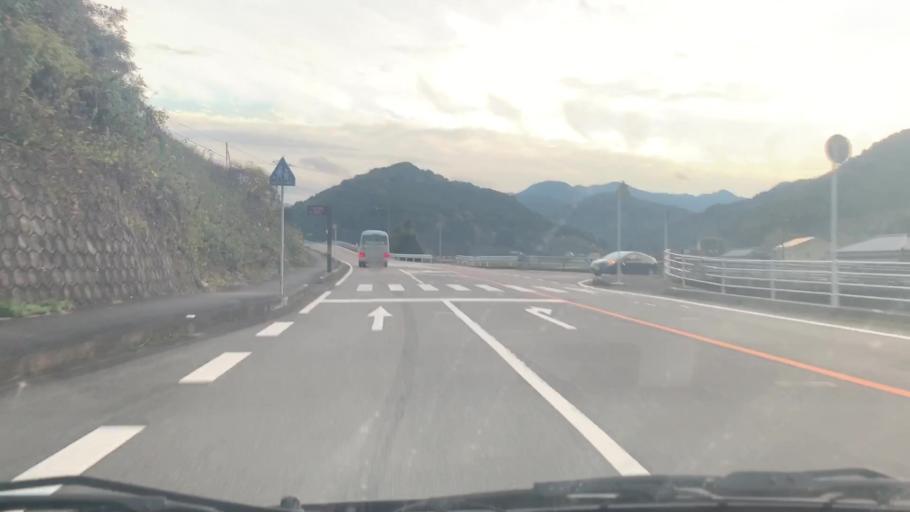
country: JP
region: Saga Prefecture
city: Kashima
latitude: 33.0779
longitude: 130.0673
